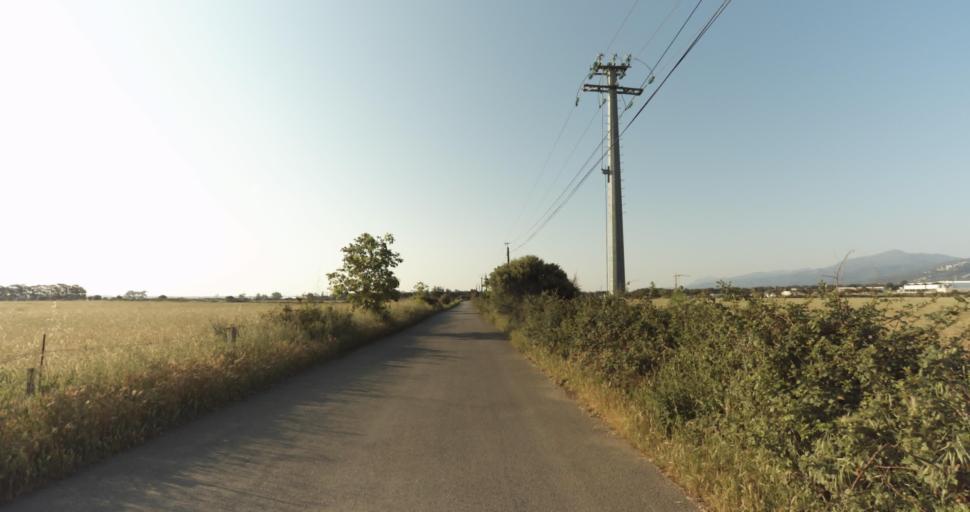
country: FR
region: Corsica
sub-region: Departement de la Haute-Corse
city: Biguglia
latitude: 42.6073
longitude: 9.4503
